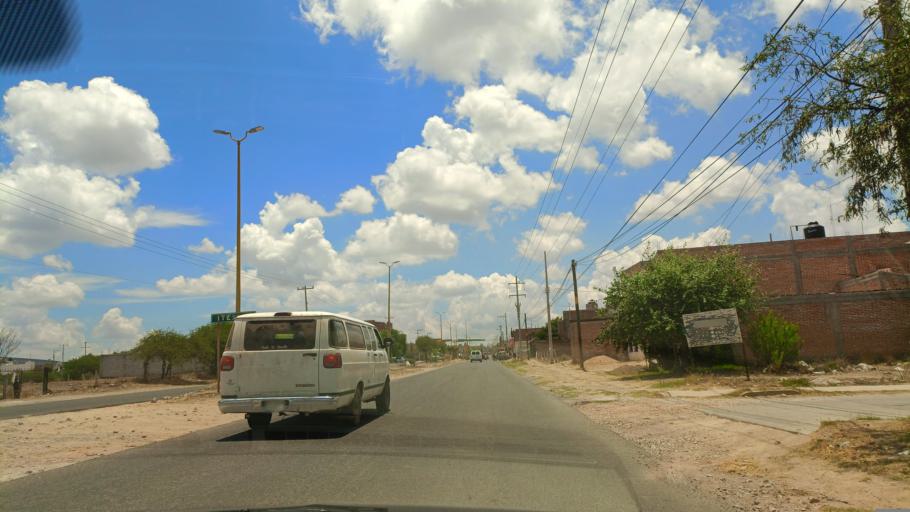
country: MX
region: Guanajuato
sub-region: San Luis de la Paz
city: San Ignacio
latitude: 21.2875
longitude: -100.5328
